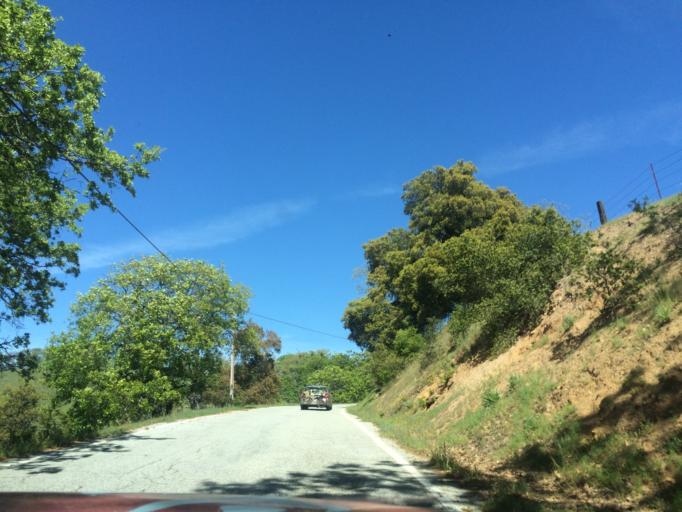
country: US
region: California
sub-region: Santa Clara County
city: Morgan Hill
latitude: 37.1814
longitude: -121.5595
